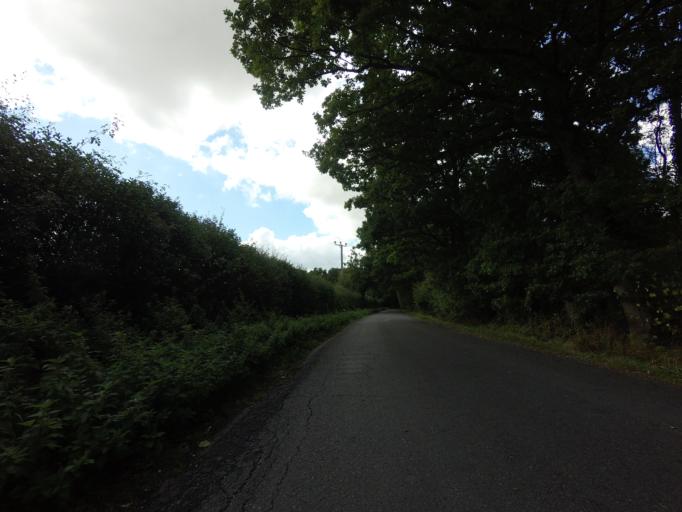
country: GB
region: England
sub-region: Kent
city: Staplehurst
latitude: 51.1524
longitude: 0.5198
